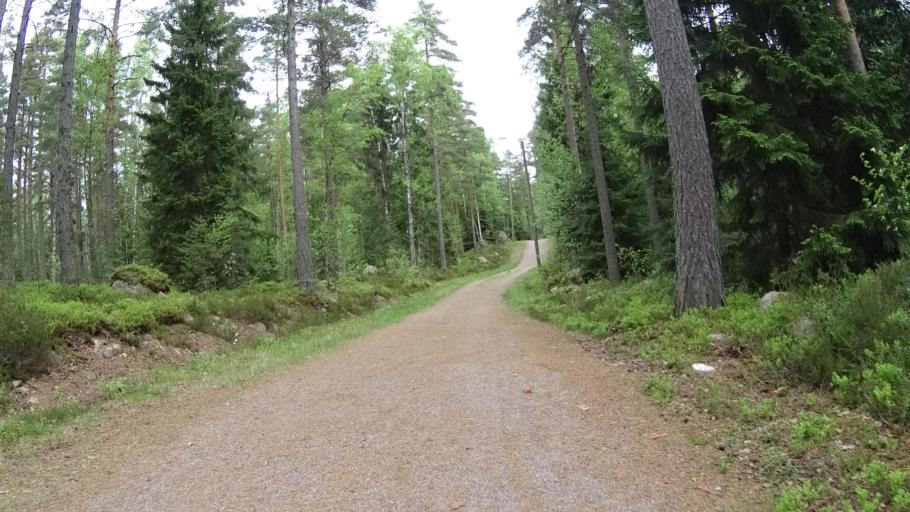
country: FI
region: Uusimaa
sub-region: Helsinki
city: Espoo
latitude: 60.2315
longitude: 24.6813
